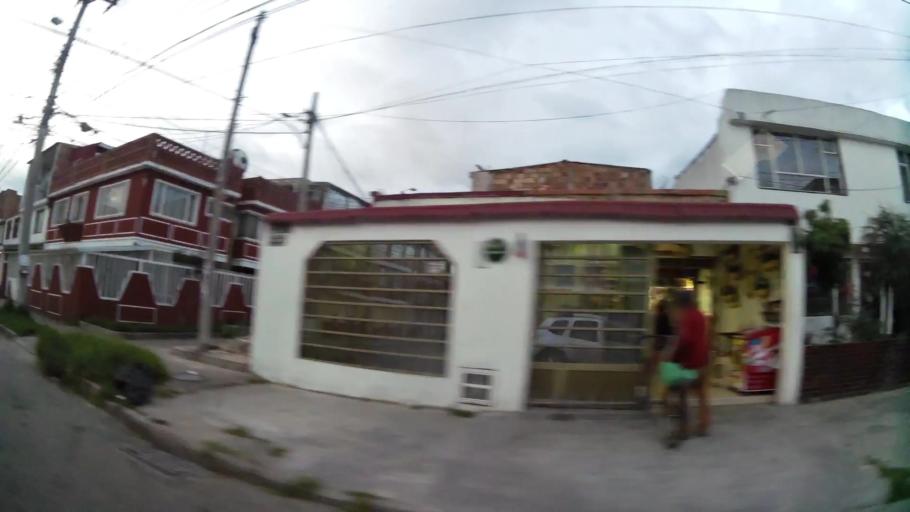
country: CO
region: Bogota D.C.
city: Bogota
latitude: 4.6081
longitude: -74.1285
